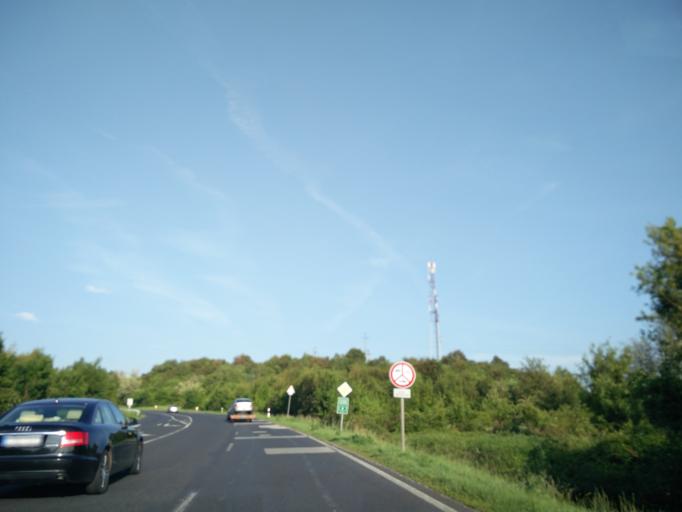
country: HU
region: Veszprem
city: Ajka
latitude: 47.1390
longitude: 17.5804
